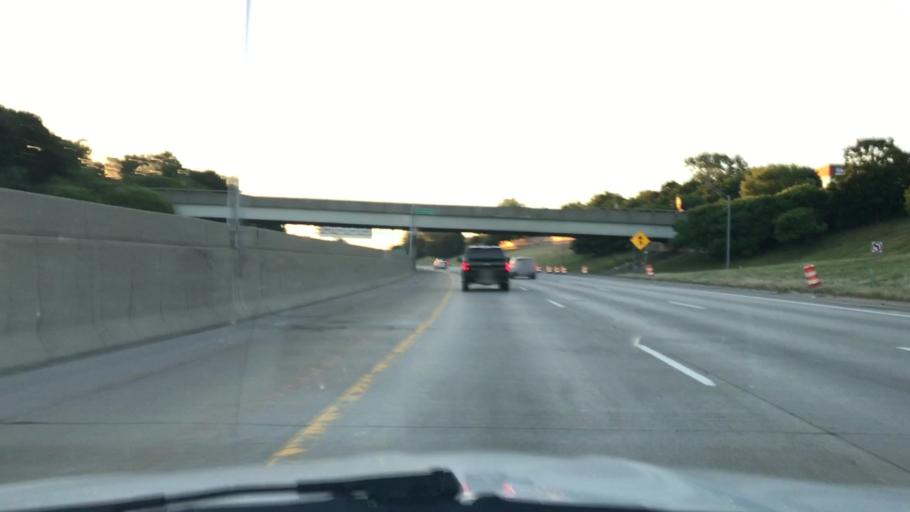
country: US
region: Michigan
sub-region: Oakland County
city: Bingham Farms
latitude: 42.4853
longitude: -83.2593
